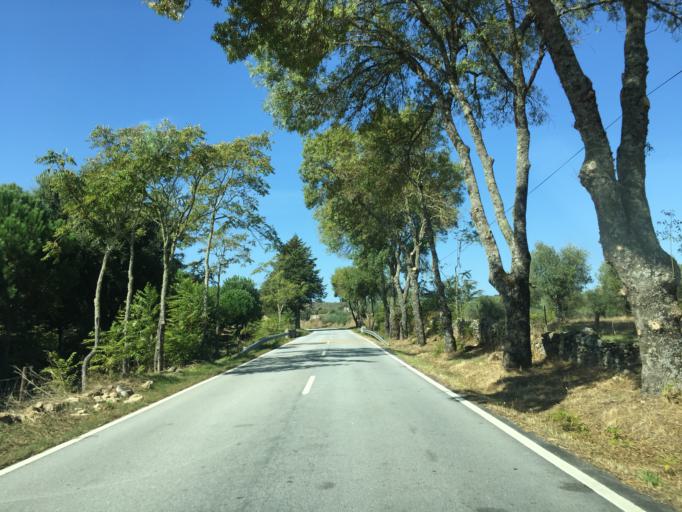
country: PT
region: Portalegre
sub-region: Portalegre
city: Alagoa
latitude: 39.4339
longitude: -7.5316
